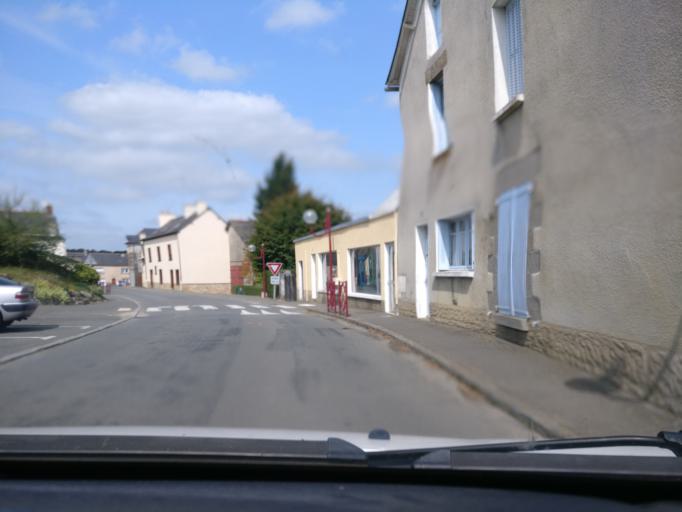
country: FR
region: Brittany
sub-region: Departement d'Ille-et-Vilaine
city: Chasne-sur-Illet
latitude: 48.2417
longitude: -1.5613
